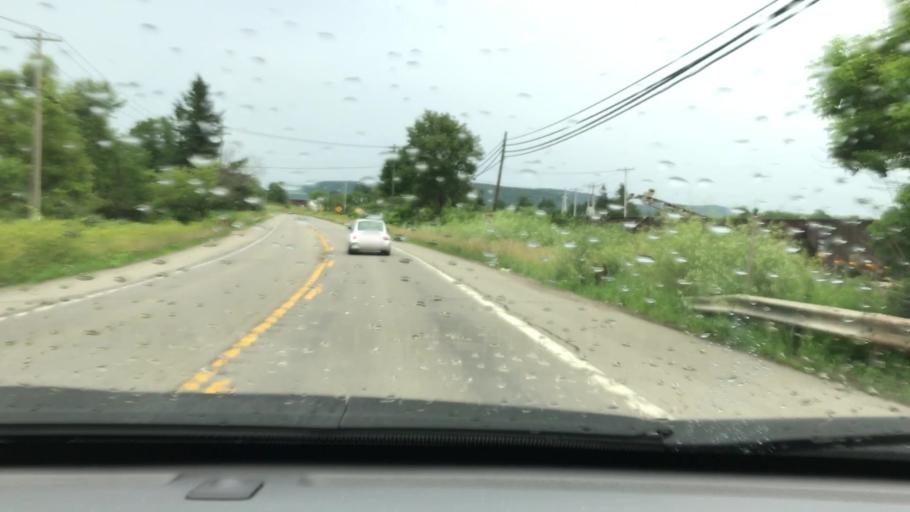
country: US
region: New York
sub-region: Cattaraugus County
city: Salamanca
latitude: 42.1904
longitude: -78.6732
